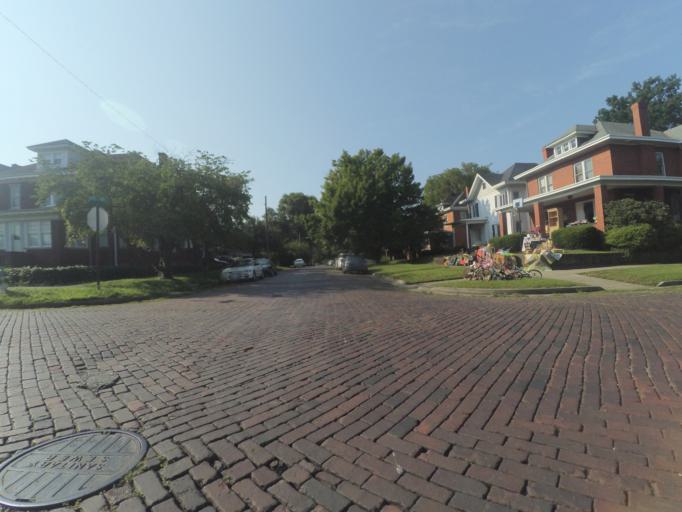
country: US
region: West Virginia
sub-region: Cabell County
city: Huntington
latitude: 38.4118
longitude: -82.4449
